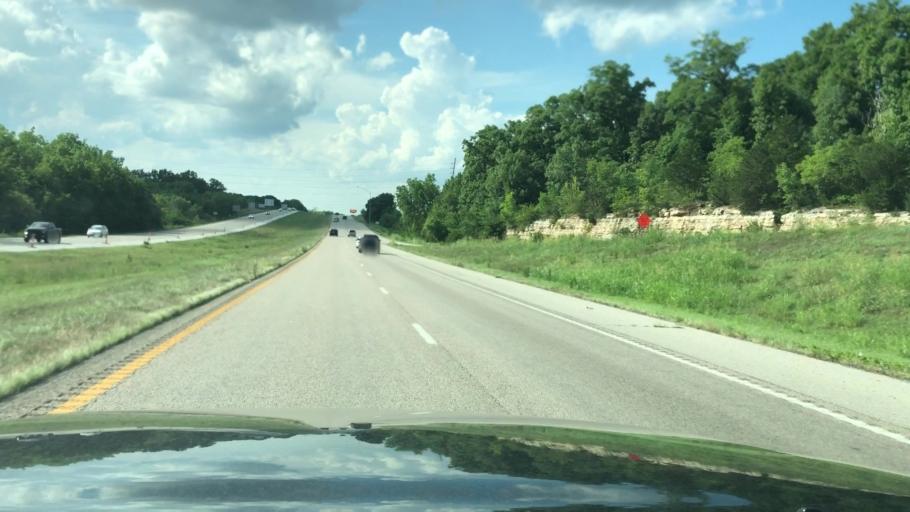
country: US
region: Missouri
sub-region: Saint Charles County
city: Wentzville
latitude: 38.8244
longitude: -90.8501
